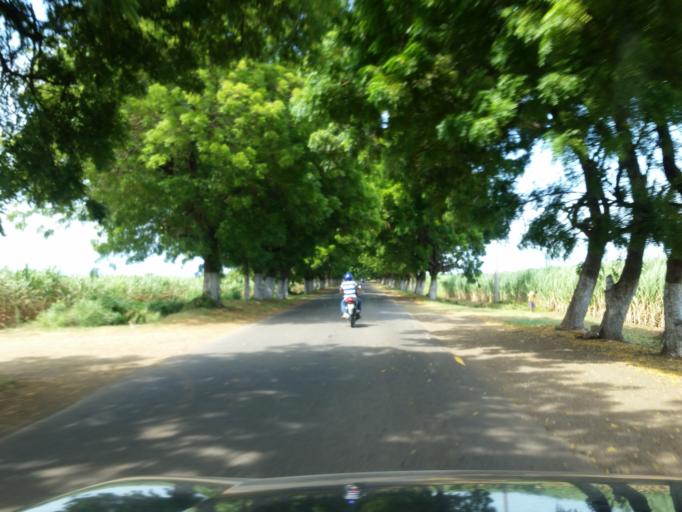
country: NI
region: Managua
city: Masachapa
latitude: 11.8044
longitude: -86.4967
